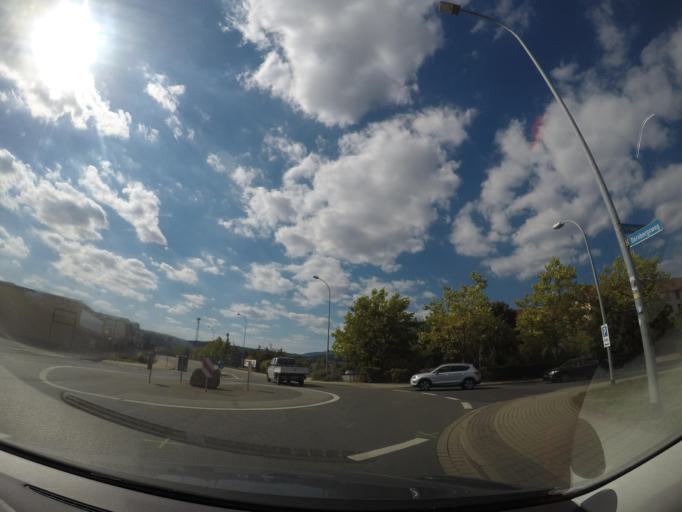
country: DE
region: Saxony-Anhalt
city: Wernigerode
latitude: 51.8466
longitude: 10.7833
